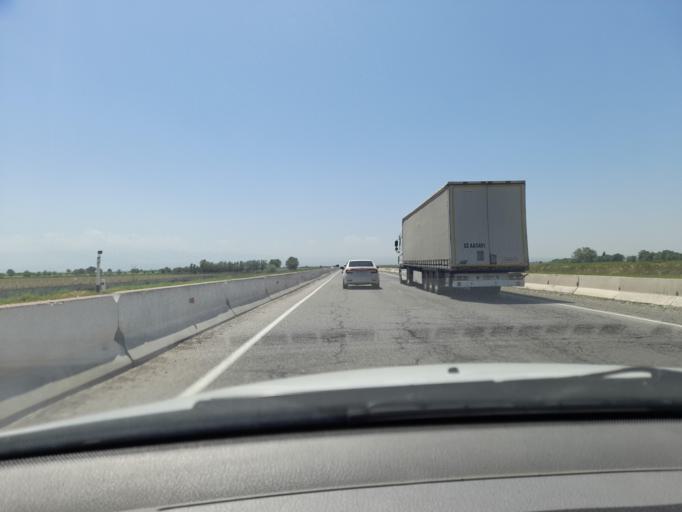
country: UZ
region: Jizzax
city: Paxtakor
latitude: 40.2347
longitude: 68.0021
